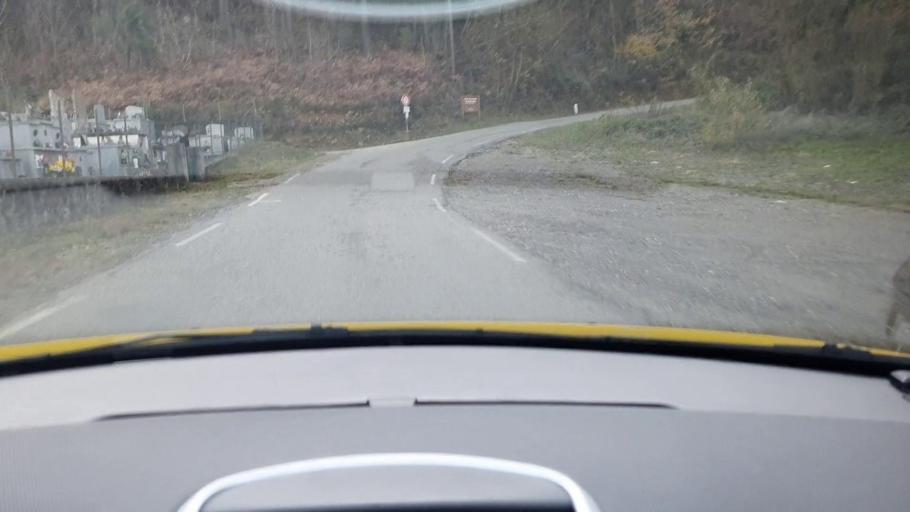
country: FR
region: Languedoc-Roussillon
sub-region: Departement du Gard
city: Branoux-les-Taillades
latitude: 44.2294
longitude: 4.0018
